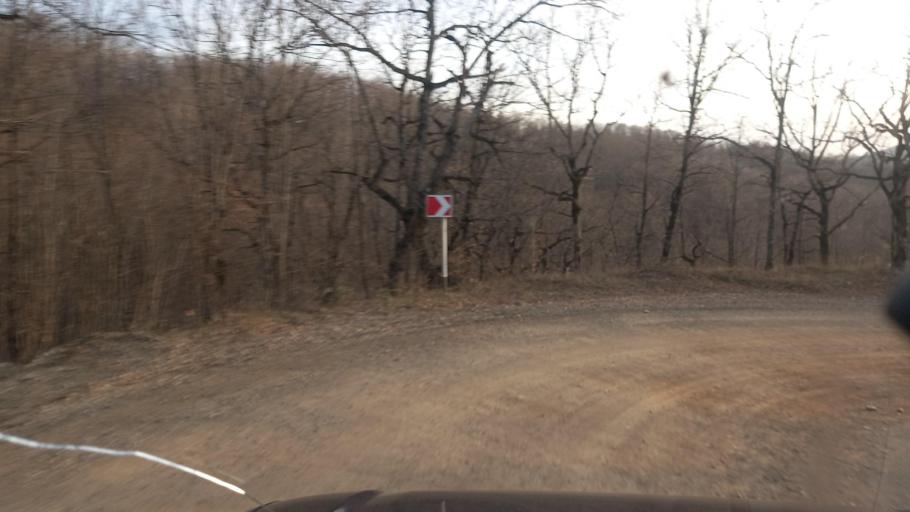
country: RU
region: Krasnodarskiy
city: Goryachiy Klyuch
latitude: 44.3687
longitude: 39.2191
